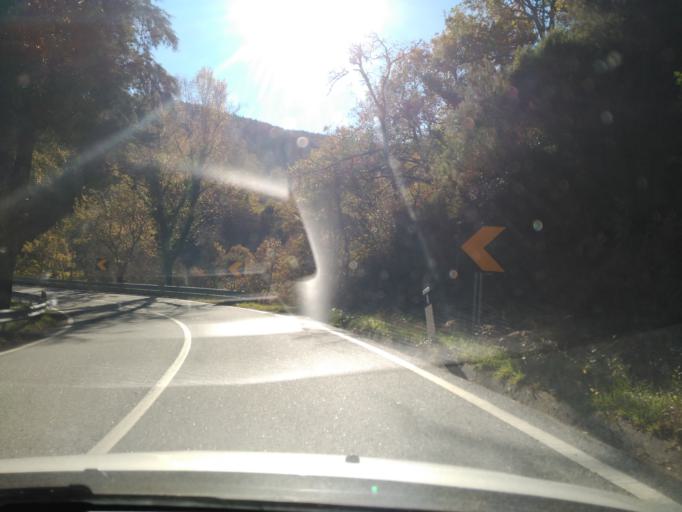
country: PT
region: Braga
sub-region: Cabeceiras de Basto
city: Cabeceiras de Basto
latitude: 41.6702
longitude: -7.9687
